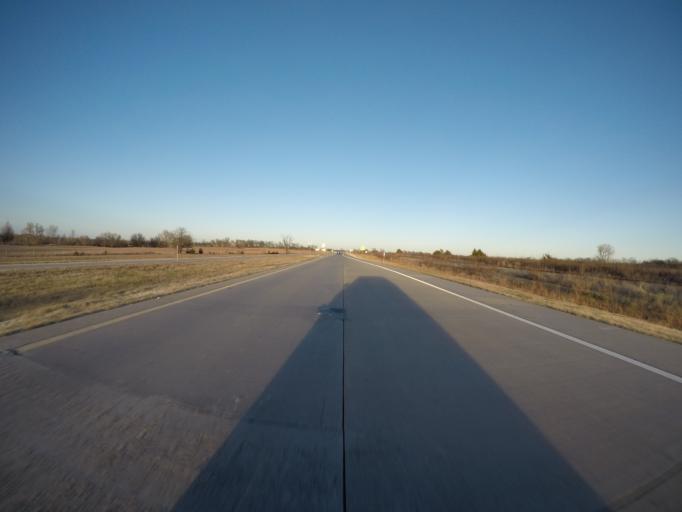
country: US
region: Kansas
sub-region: Harvey County
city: North Newton
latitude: 38.0685
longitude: -97.3082
